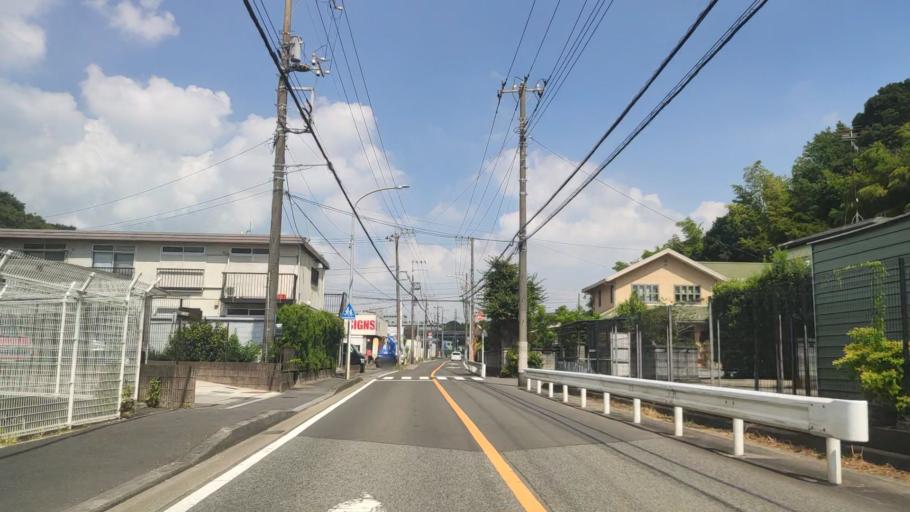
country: JP
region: Kanagawa
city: Minami-rinkan
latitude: 35.4435
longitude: 139.5066
